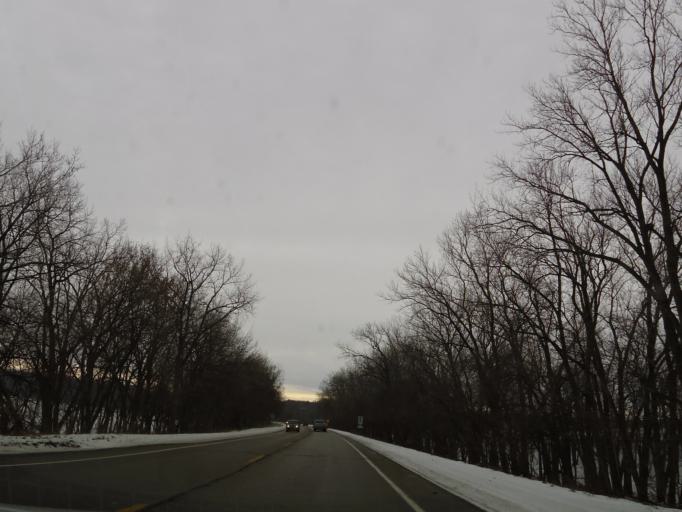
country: US
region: Illinois
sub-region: LaSalle County
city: Peru
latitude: 41.3183
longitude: -89.1199
